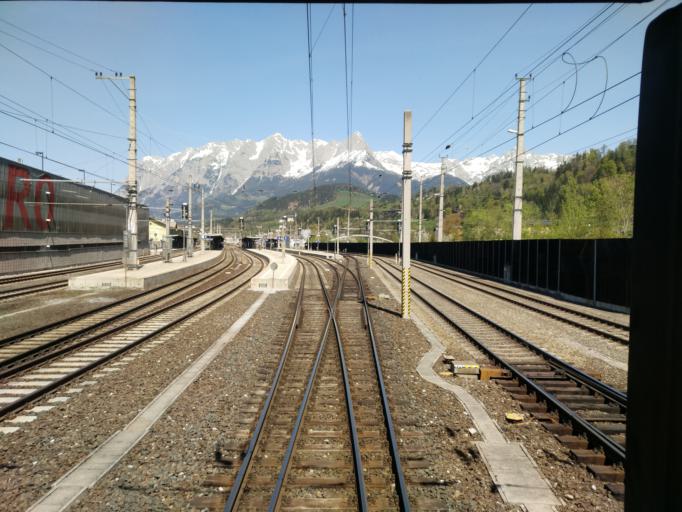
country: AT
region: Salzburg
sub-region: Politischer Bezirk Sankt Johann im Pongau
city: Bischofshofen
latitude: 47.4154
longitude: 13.2202
